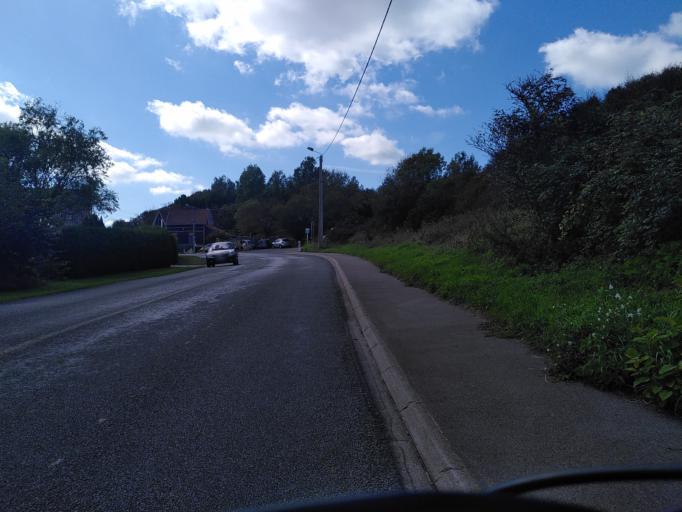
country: FR
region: Nord-Pas-de-Calais
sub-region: Departement du Pas-de-Calais
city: Wimille
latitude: 50.7805
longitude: 1.6295
